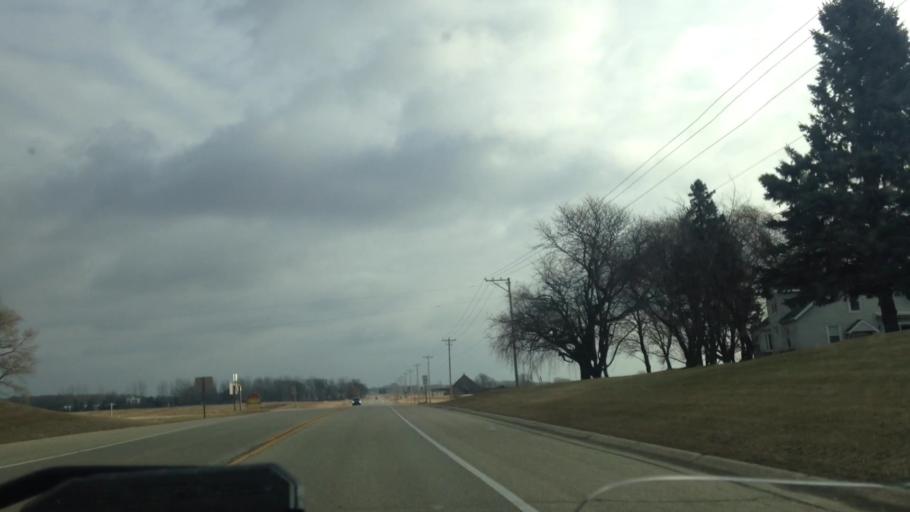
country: US
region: Wisconsin
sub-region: Dodge County
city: Juneau
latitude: 43.4452
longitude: -88.7434
